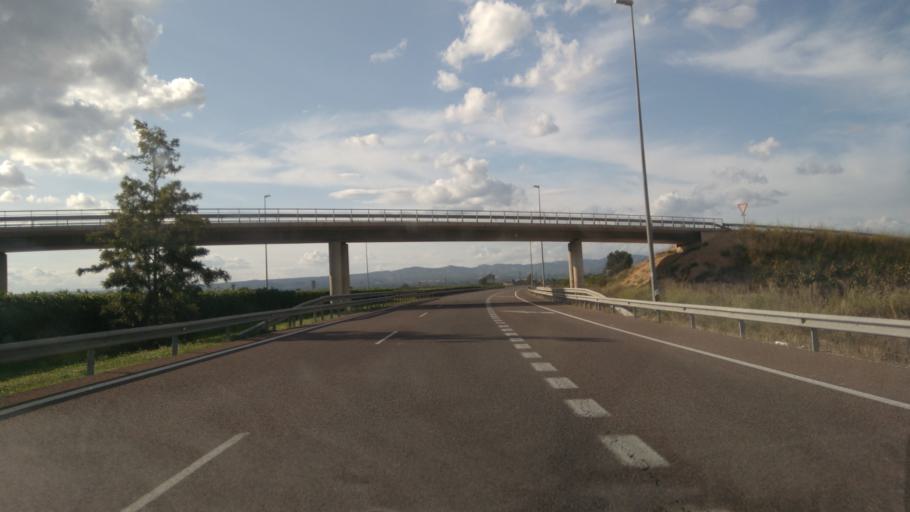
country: ES
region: Valencia
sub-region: Provincia de Valencia
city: Guadassuar
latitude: 39.1780
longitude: -0.4792
